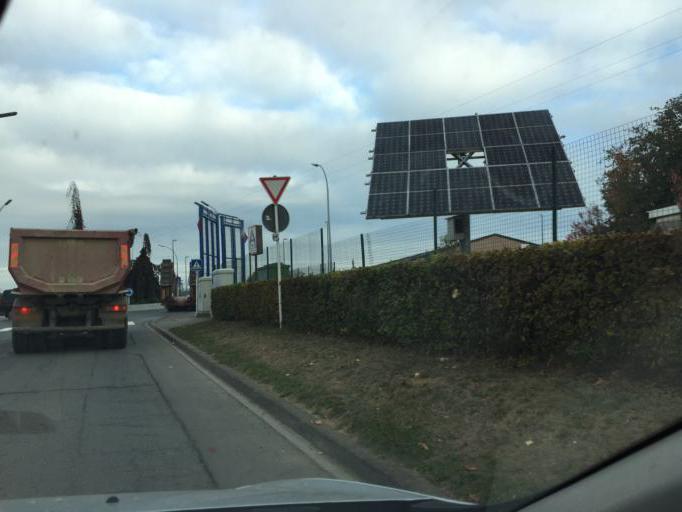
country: LU
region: Luxembourg
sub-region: Canton de Mersch
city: Mersch
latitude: 49.7587
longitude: 6.0992
